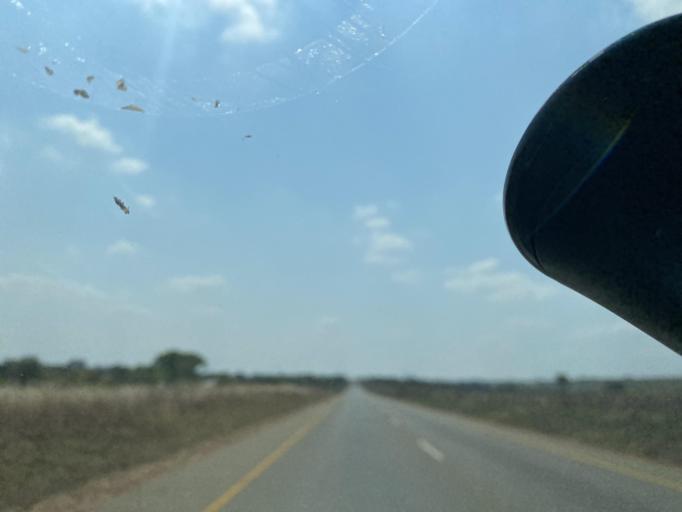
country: ZM
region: Lusaka
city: Chongwe
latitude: -15.5420
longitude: 28.6615
